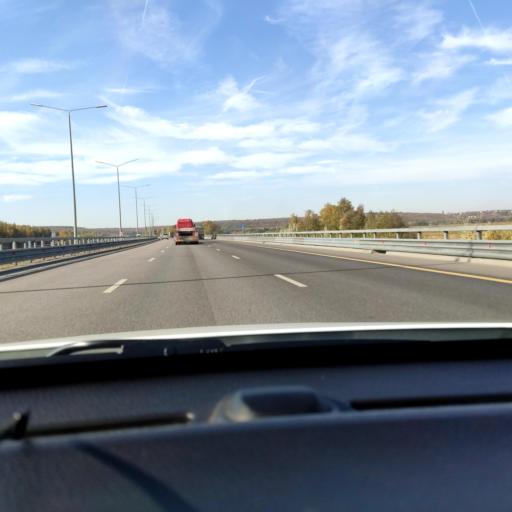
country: RU
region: Voronezj
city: Somovo
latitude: 51.7873
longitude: 39.2824
